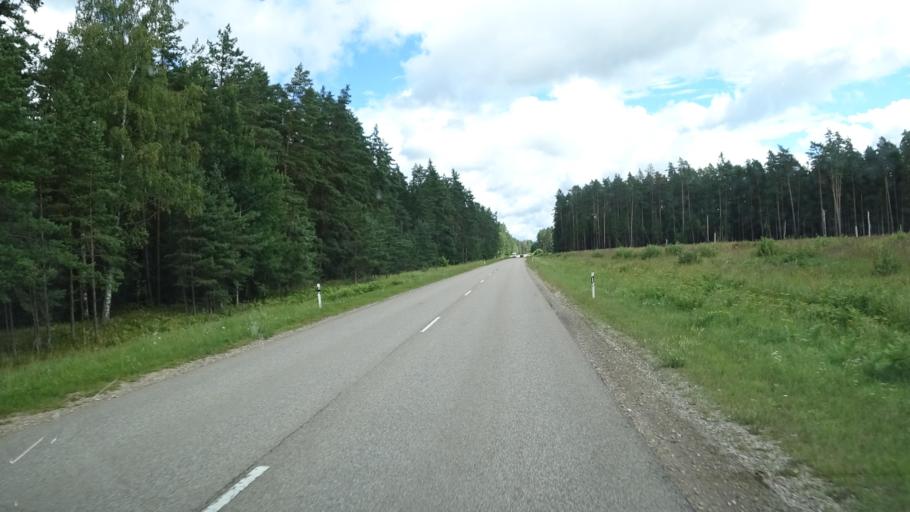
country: LV
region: Pavilostas
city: Pavilosta
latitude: 56.7267
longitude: 21.1990
